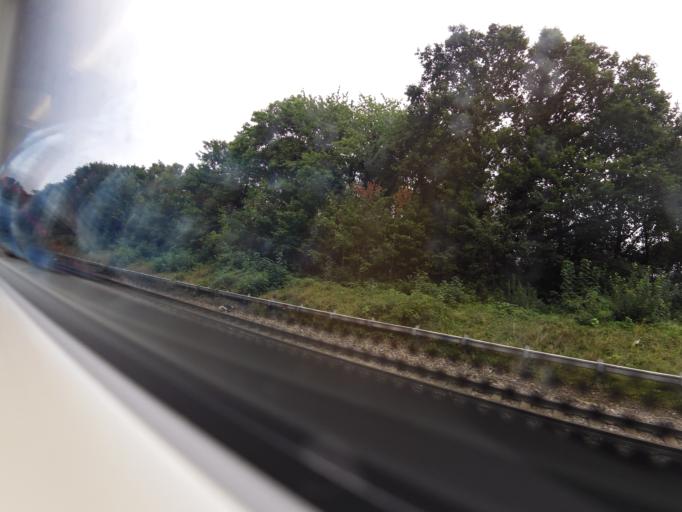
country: GB
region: England
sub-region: Greater London
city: Catford
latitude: 51.4659
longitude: -0.0374
